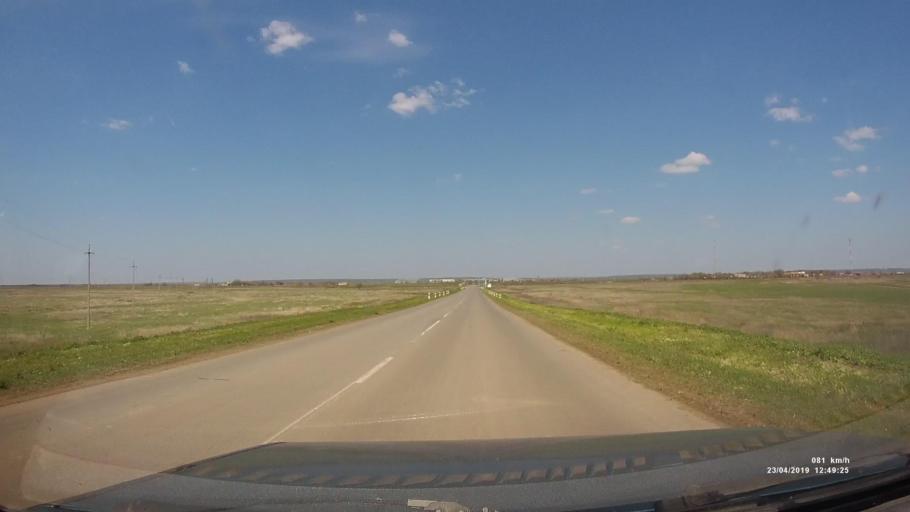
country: RU
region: Kalmykiya
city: Yashalta
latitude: 46.5369
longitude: 42.6392
